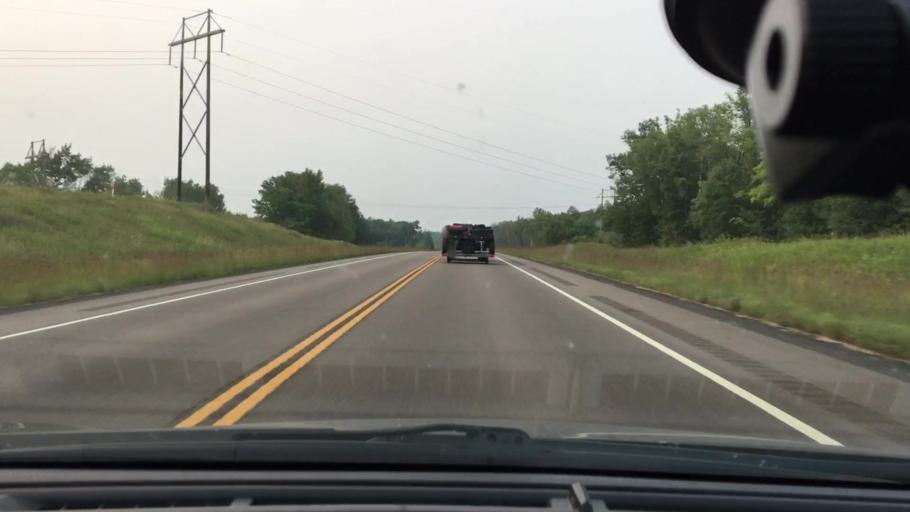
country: US
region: Minnesota
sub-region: Crow Wing County
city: Crosby
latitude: 46.6020
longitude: -93.9520
